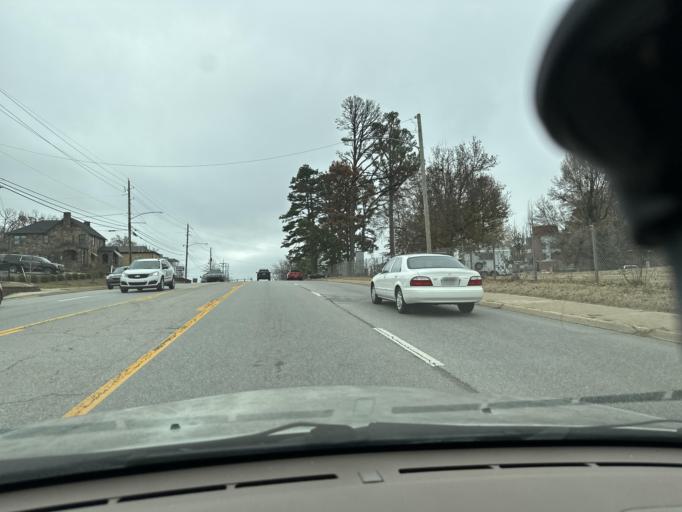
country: US
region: Arkansas
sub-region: Washington County
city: Fayetteville
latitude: 36.0794
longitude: -94.1570
